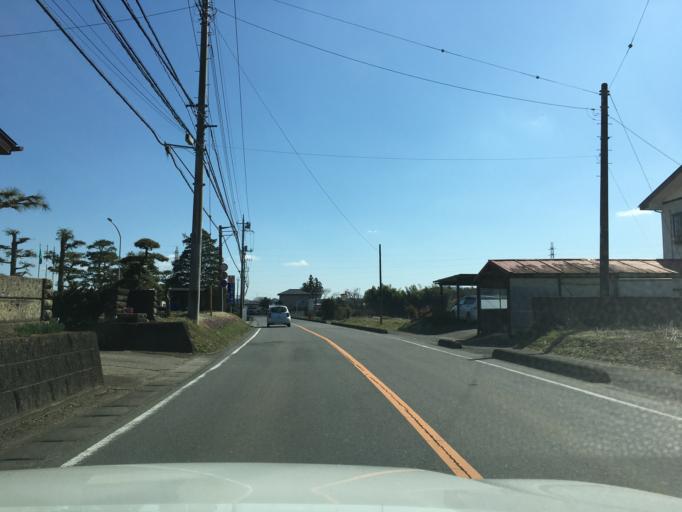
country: JP
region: Tochigi
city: Karasuyama
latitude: 36.7441
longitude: 140.1337
